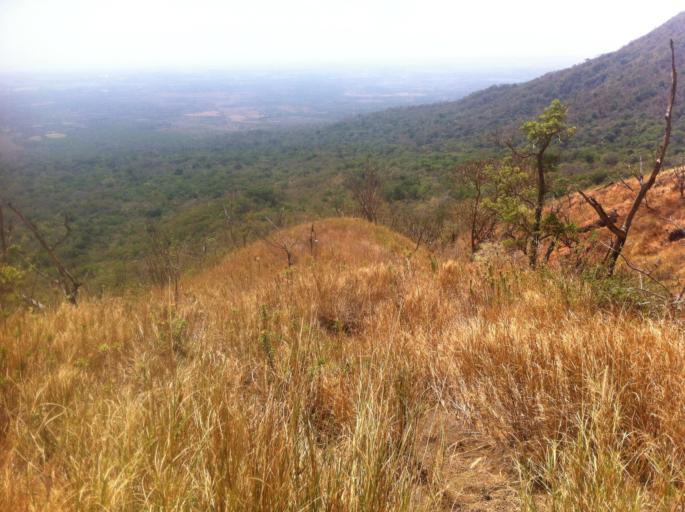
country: NI
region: Chinandega
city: Chichigalpa
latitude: 12.6966
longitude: -87.0209
